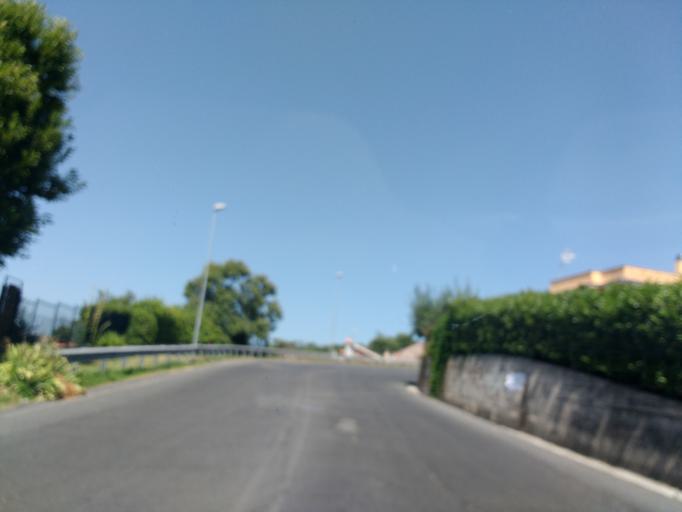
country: IT
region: Latium
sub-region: Citta metropolitana di Roma Capitale
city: Rocca di Papa
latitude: 41.7699
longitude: 12.7063
